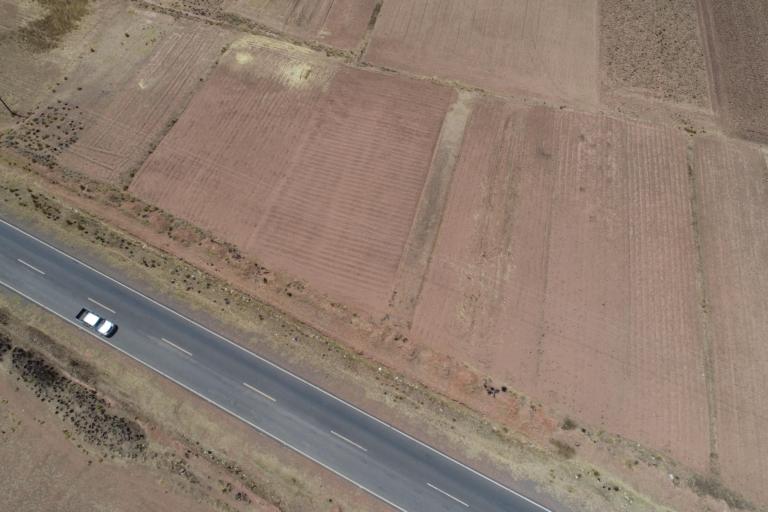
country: BO
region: La Paz
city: Achacachi
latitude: -15.9097
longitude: -68.8881
